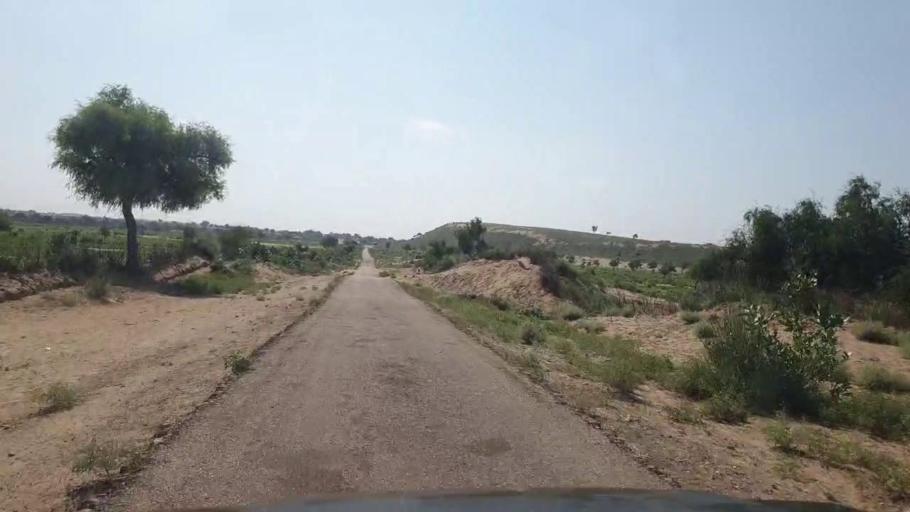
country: PK
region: Sindh
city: Islamkot
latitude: 25.1647
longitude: 70.4039
